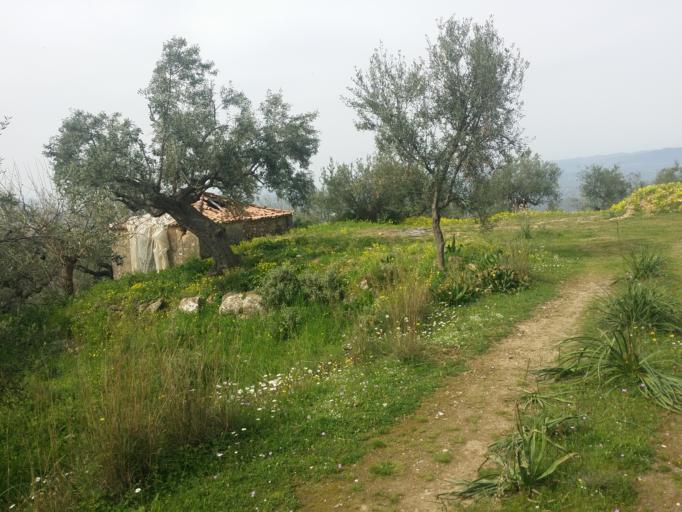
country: GR
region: Peloponnese
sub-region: Nomos Messinias
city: Thouria
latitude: 37.1101
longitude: 22.0497
